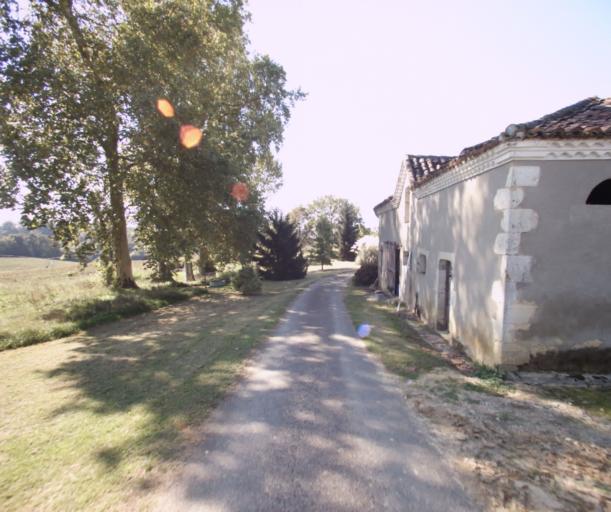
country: FR
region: Aquitaine
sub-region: Departement des Landes
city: Gabarret
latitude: 43.9466
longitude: 0.0025
